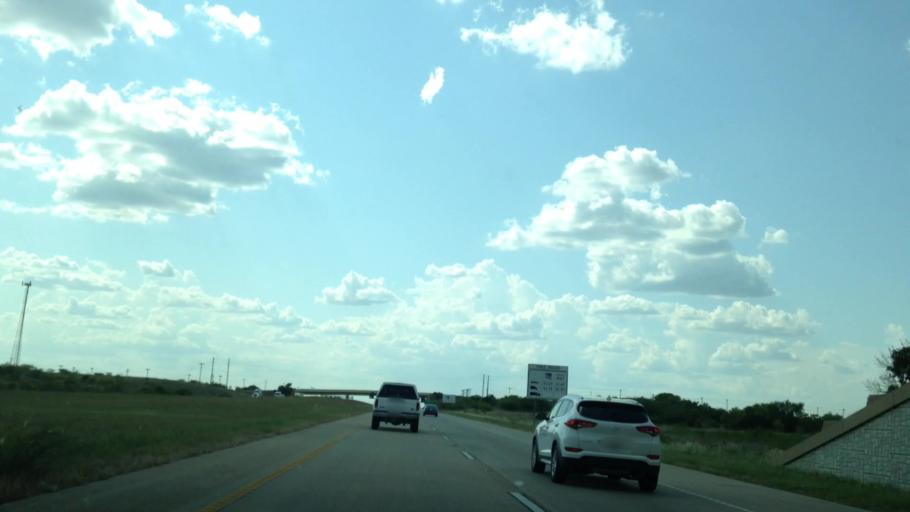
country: US
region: Texas
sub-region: Travis County
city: Onion Creek
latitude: 30.0929
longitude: -97.7564
